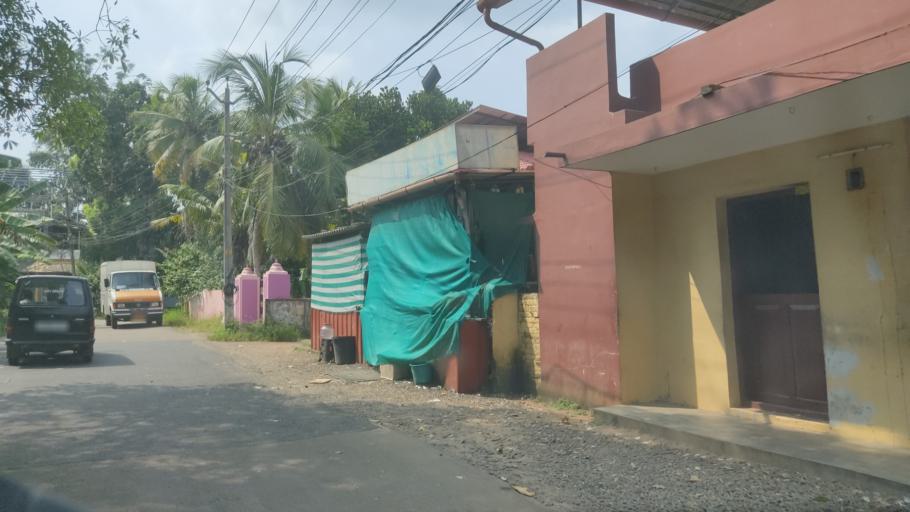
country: IN
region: Kerala
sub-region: Pattanamtitta
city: Tiruvalla
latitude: 9.3322
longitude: 76.5318
